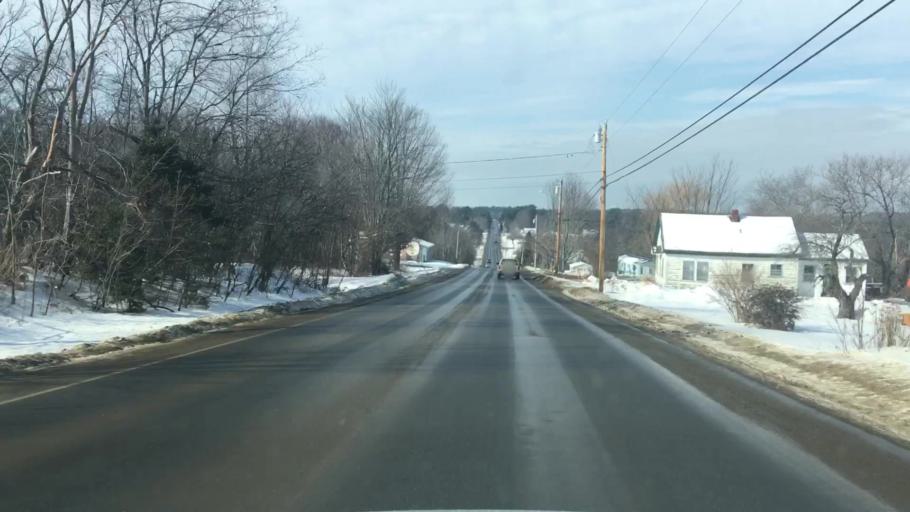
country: US
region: Maine
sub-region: Penobscot County
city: Hermon
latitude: 44.8485
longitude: -68.8746
